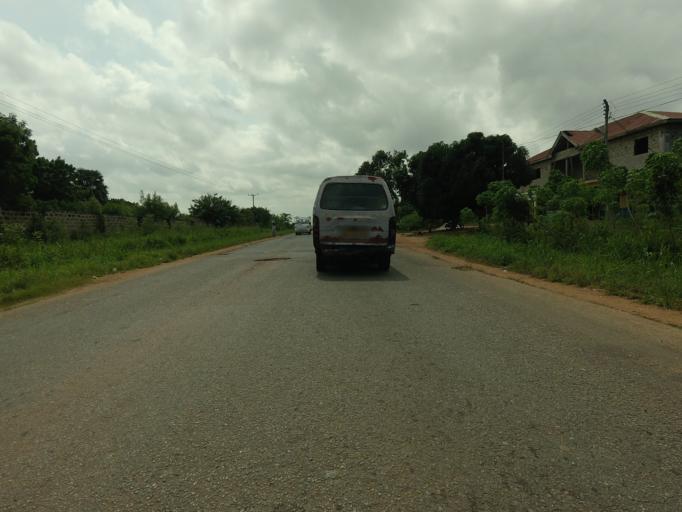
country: TG
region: Maritime
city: Lome
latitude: 6.1258
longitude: 1.1258
